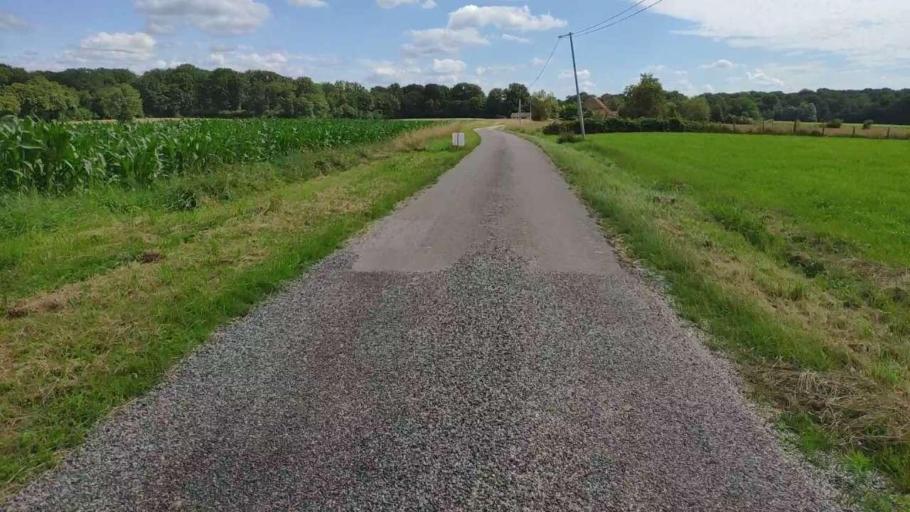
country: FR
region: Franche-Comte
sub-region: Departement du Jura
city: Bletterans
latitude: 46.8120
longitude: 5.4273
